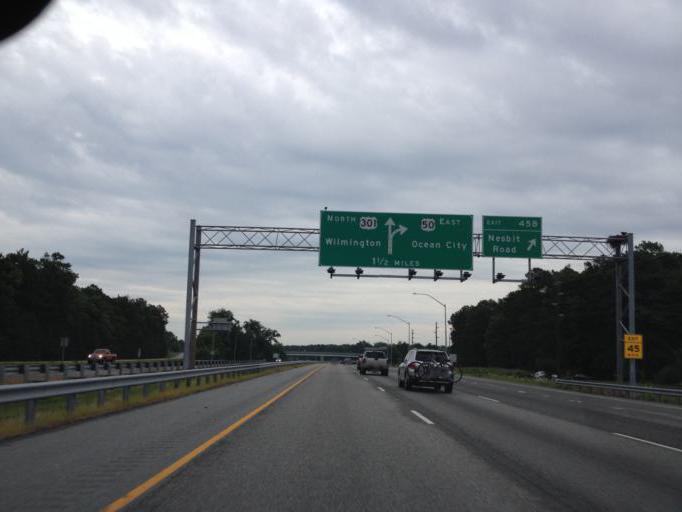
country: US
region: Maryland
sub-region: Queen Anne's County
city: Grasonville
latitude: 38.9661
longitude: -76.1900
